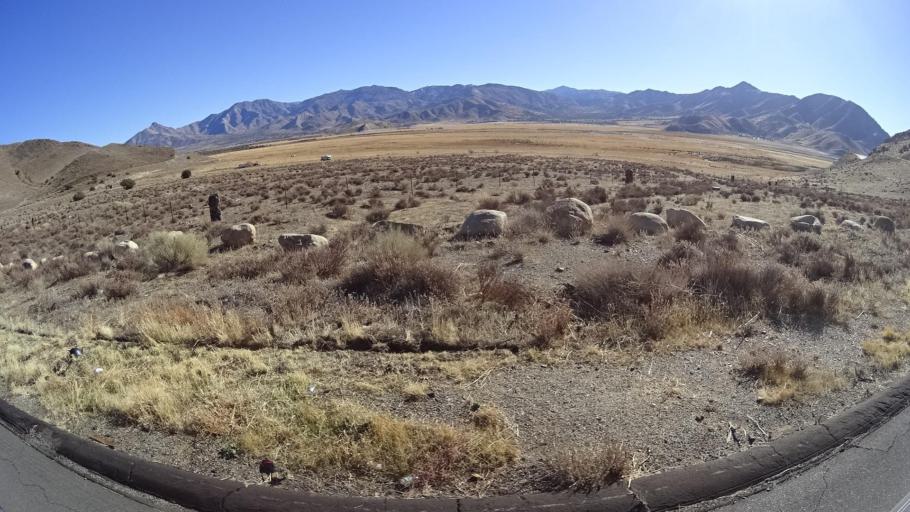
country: US
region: California
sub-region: Kern County
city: Wofford Heights
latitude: 35.6810
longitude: -118.4113
